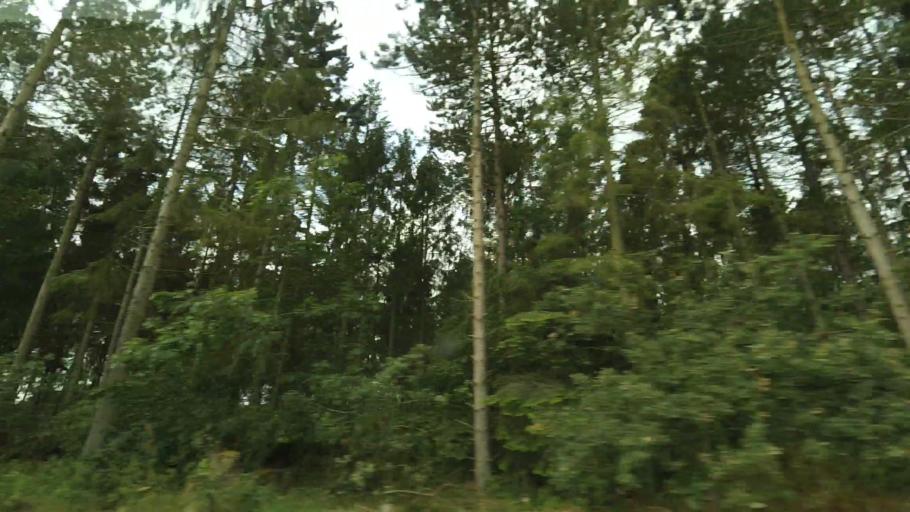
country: DK
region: Central Jutland
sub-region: Syddjurs Kommune
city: Ryomgard
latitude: 56.3606
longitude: 10.5132
